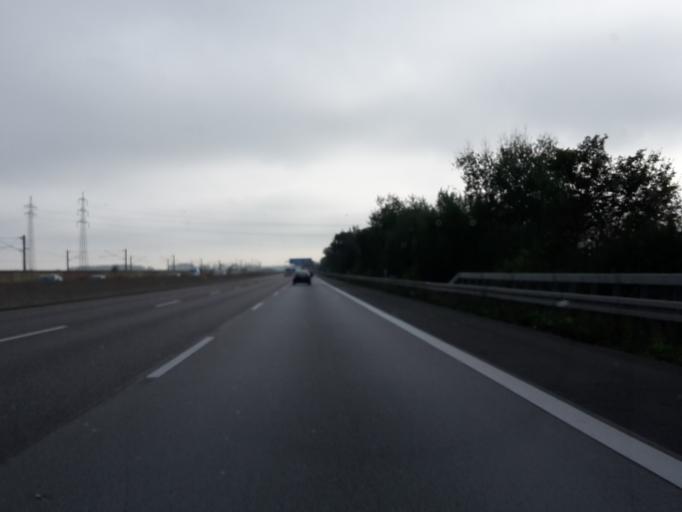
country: DE
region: Hesse
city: Raunheim
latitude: 50.0347
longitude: 8.4412
